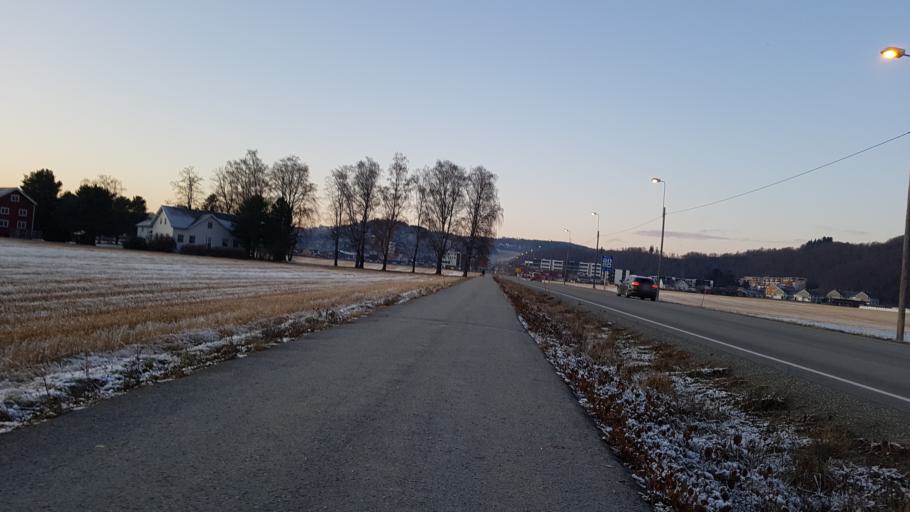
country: NO
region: Sor-Trondelag
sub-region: Melhus
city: Melhus
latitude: 63.2794
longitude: 10.2885
